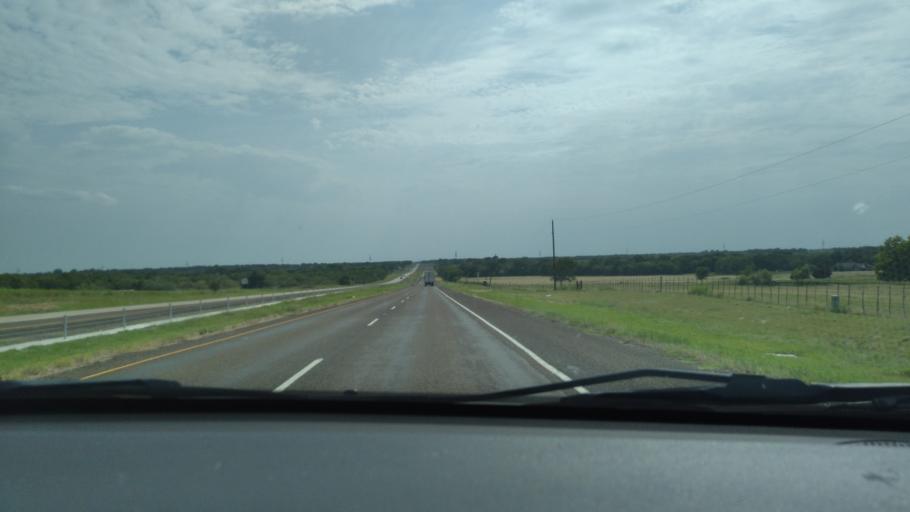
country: US
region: Texas
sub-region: Navarro County
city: Corsicana
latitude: 32.0345
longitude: -96.5541
